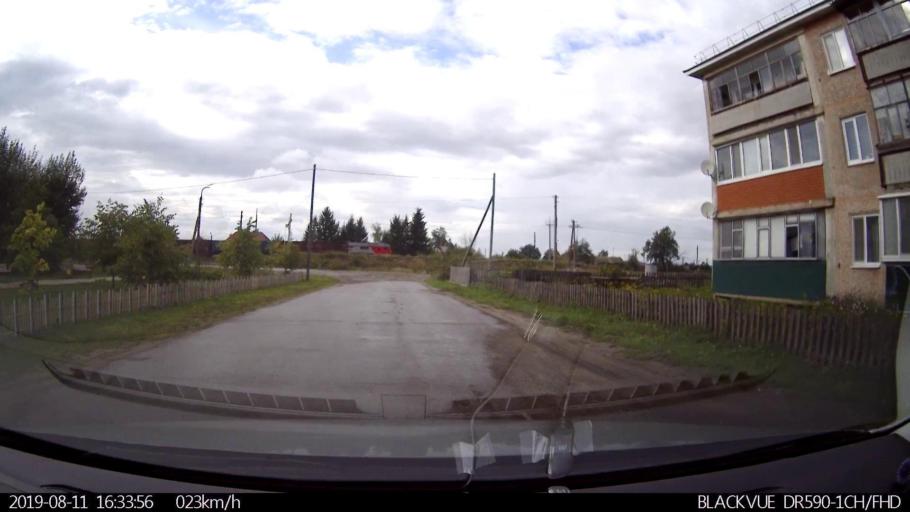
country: RU
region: Ulyanovsk
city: Mayna
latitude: 54.1163
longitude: 47.6238
